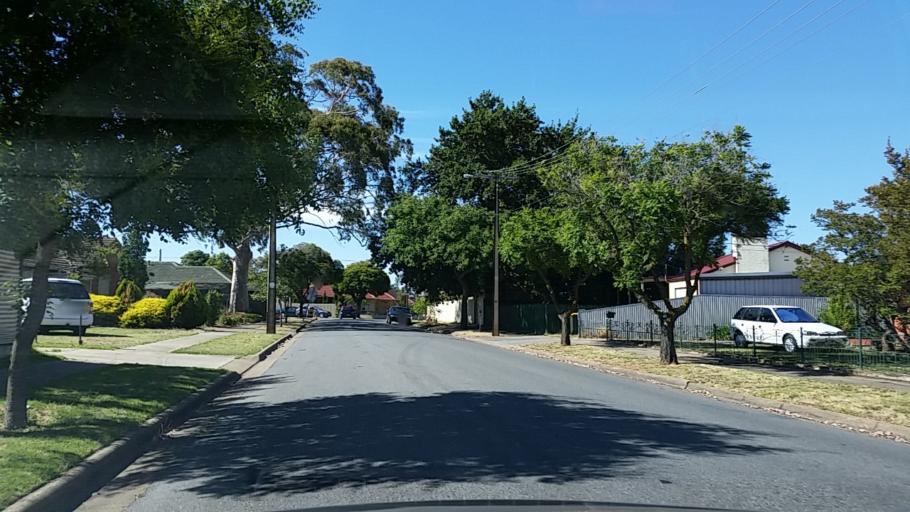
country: AU
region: South Australia
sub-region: Charles Sturt
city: Woodville West
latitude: -34.8913
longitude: 138.5345
